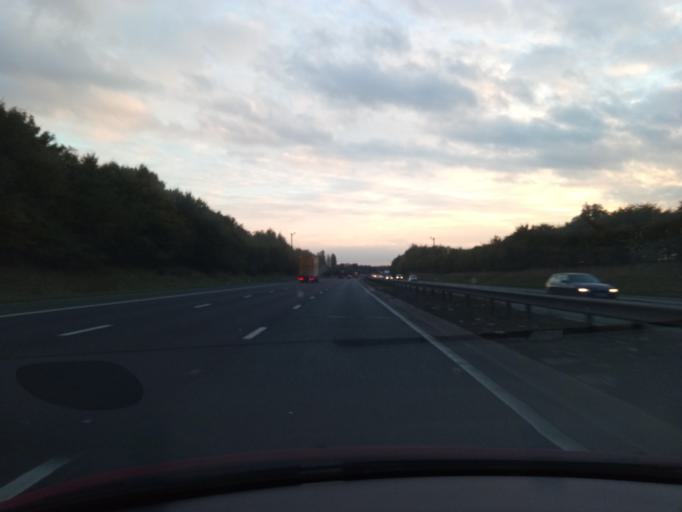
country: GB
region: England
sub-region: City and Borough of Leeds
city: Wetherby
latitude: 53.9838
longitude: -1.3628
